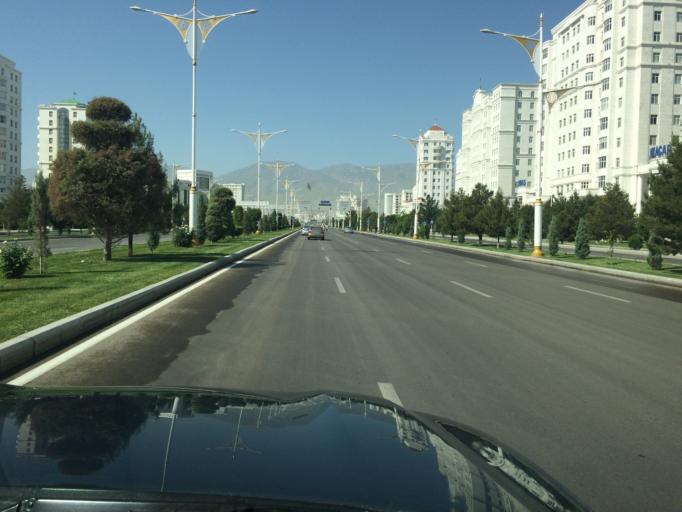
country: TM
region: Ahal
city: Ashgabat
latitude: 37.9021
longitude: 58.3638
